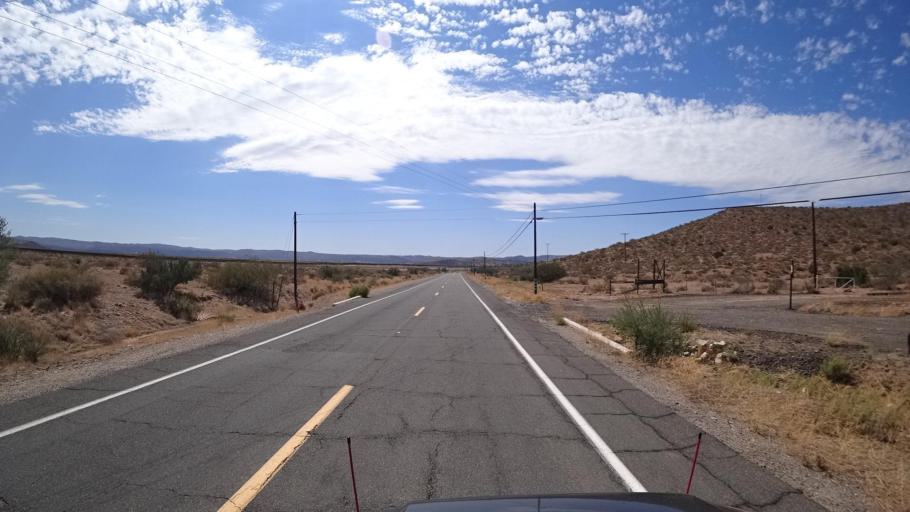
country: MX
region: Baja California
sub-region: Tecate
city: Cereso del Hongo
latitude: 32.6198
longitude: -116.1608
